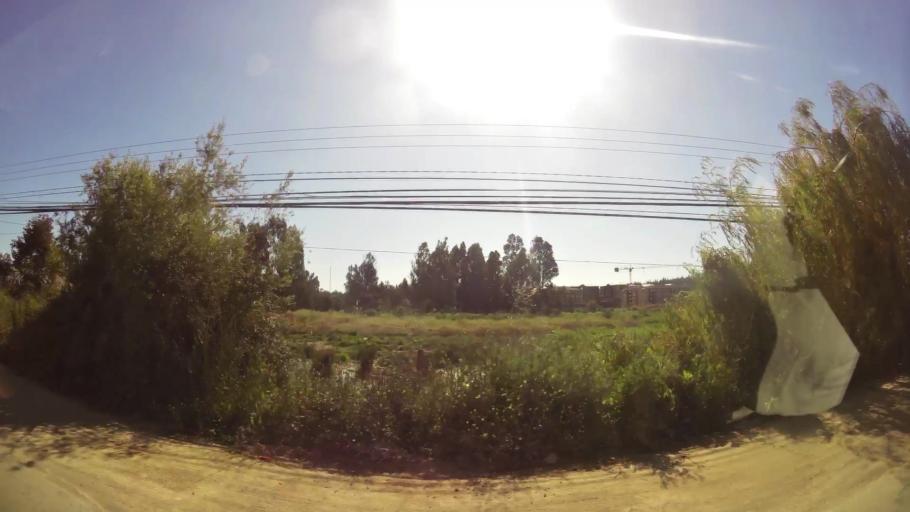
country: CL
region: Valparaiso
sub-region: Provincia de Valparaiso
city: Vina del Mar
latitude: -33.1351
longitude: -71.5637
